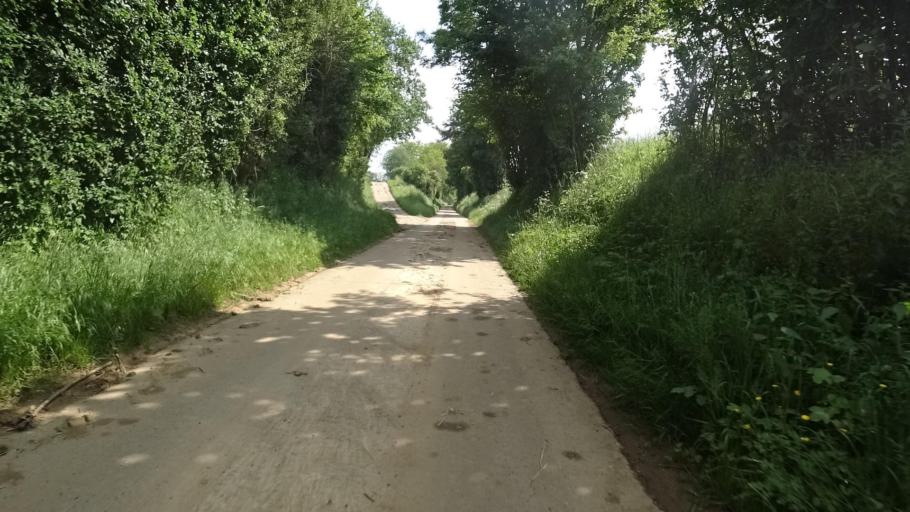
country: BE
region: Wallonia
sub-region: Province du Brabant Wallon
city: Walhain-Saint-Paul
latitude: 50.6624
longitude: 4.6653
